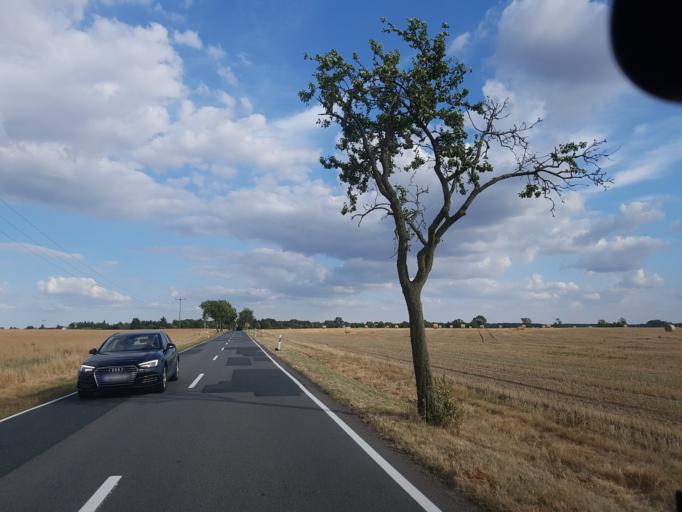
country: DE
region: Brandenburg
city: Schlieben
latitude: 51.7311
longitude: 13.3085
